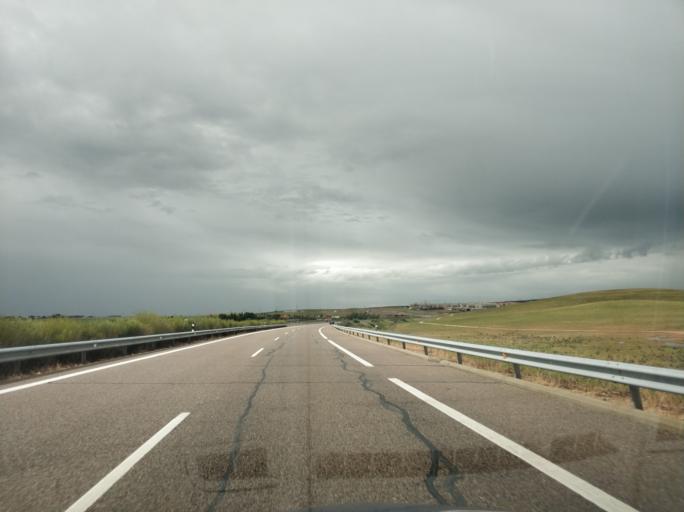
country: ES
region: Castille and Leon
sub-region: Provincia de Salamanca
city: Aldeatejada
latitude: 40.9293
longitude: -5.6778
